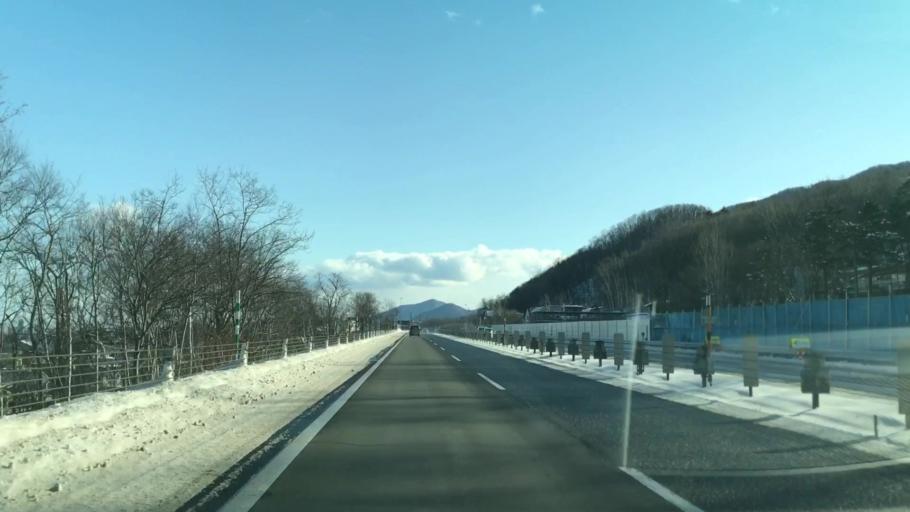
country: JP
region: Hokkaido
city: Sapporo
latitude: 43.1128
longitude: 141.2378
